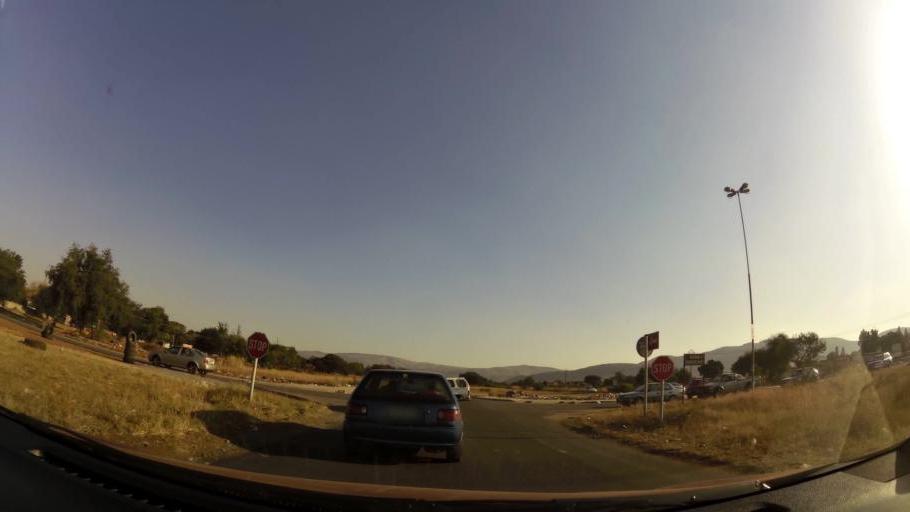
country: ZA
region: North-West
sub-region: Bojanala Platinum District Municipality
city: Rustenburg
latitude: -25.6482
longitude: 27.2257
